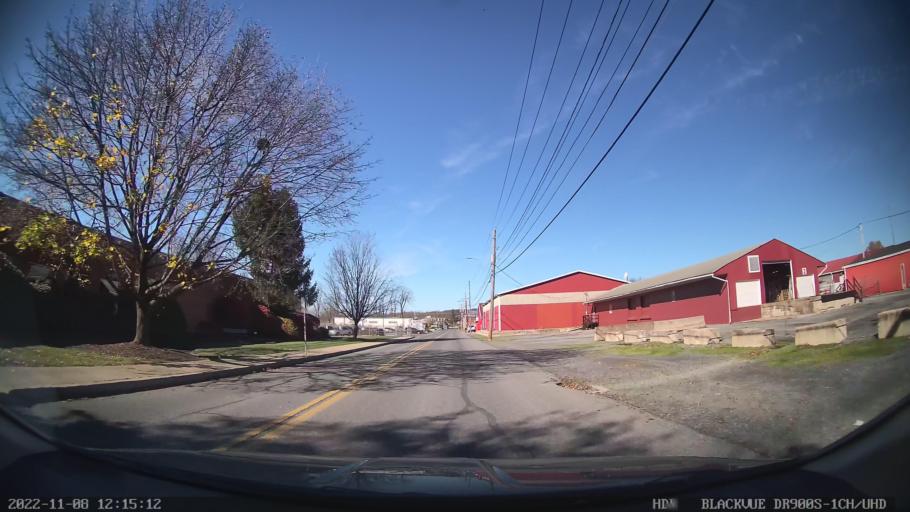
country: US
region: Pennsylvania
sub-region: Berks County
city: Kutztown
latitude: 40.5183
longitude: -75.7711
